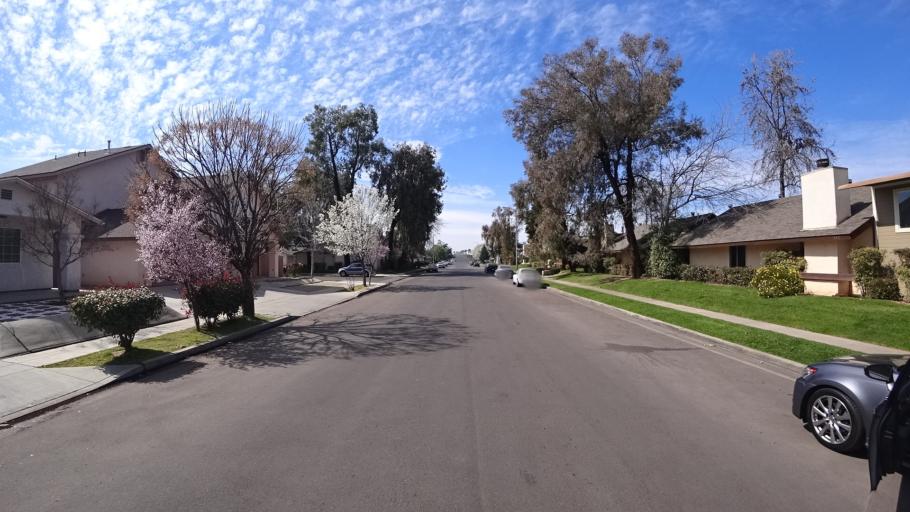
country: US
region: California
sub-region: Fresno County
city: Clovis
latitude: 36.8483
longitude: -119.7805
